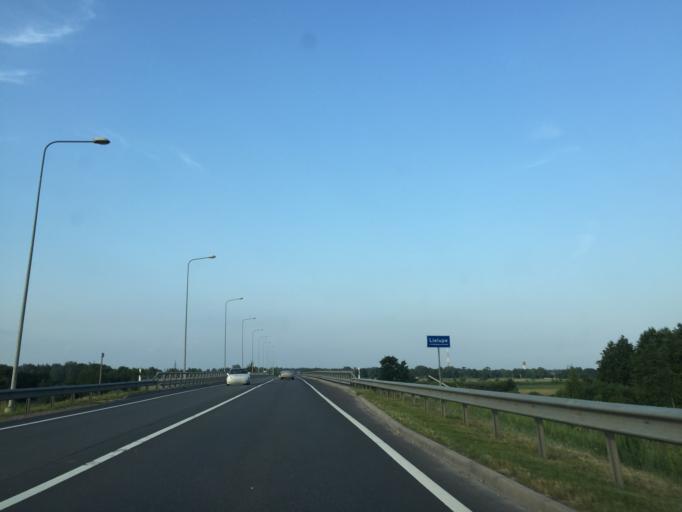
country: LV
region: Ozolnieku
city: Ozolnieki
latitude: 56.6443
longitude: 23.7853
